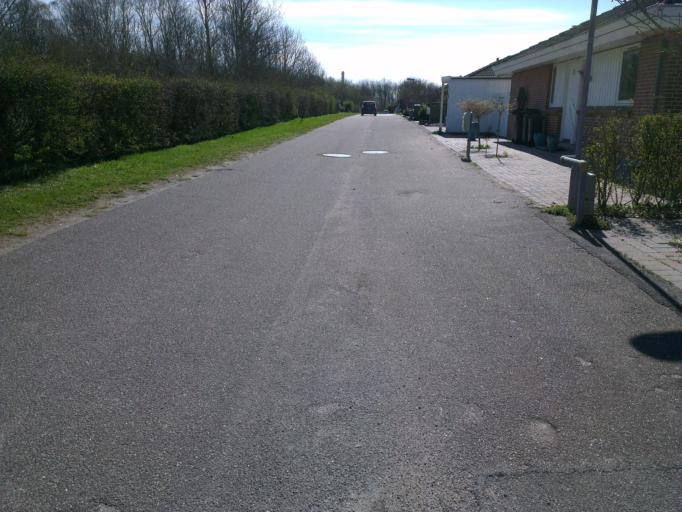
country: DK
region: Capital Region
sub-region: Frederikssund Kommune
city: Frederikssund
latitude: 55.8571
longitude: 12.0483
